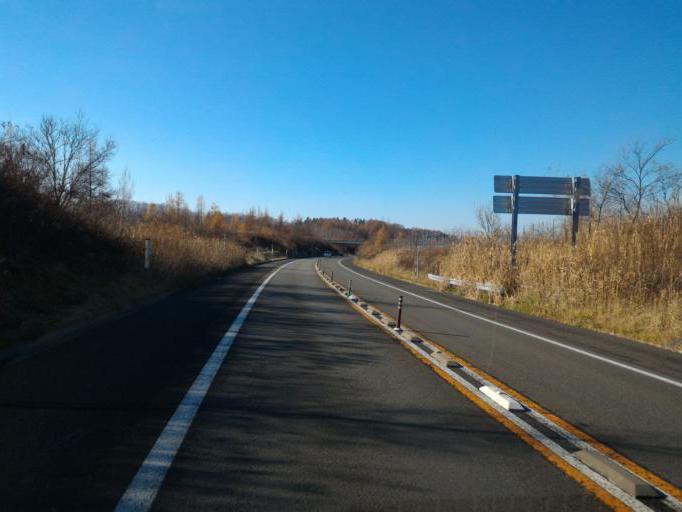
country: JP
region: Hokkaido
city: Chitose
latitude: 42.8956
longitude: 141.8652
